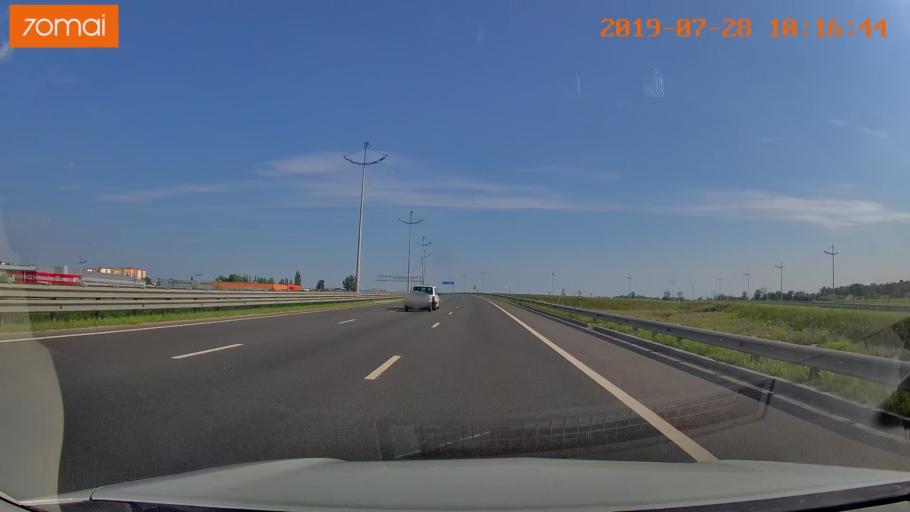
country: RU
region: Kaliningrad
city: Bol'shoe Isakovo
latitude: 54.7300
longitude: 20.5977
